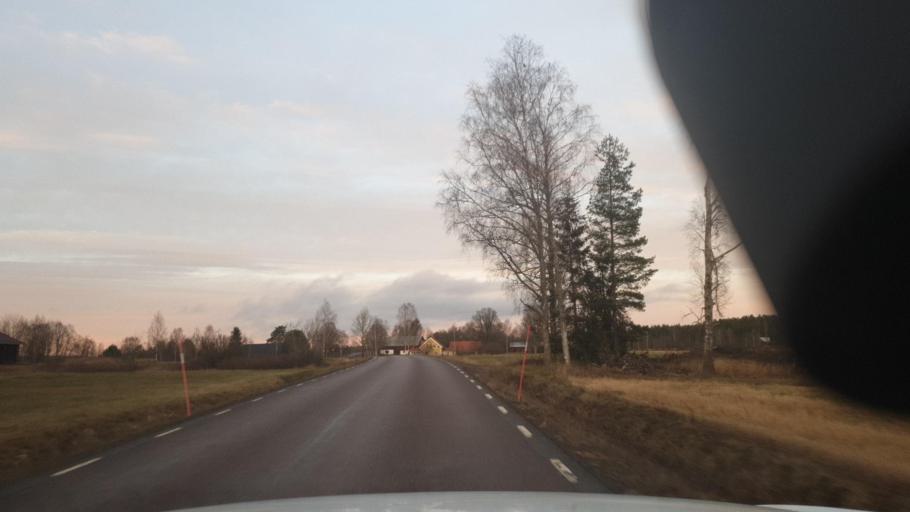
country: SE
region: Vaermland
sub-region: Eda Kommun
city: Charlottenberg
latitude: 59.7735
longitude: 12.2100
